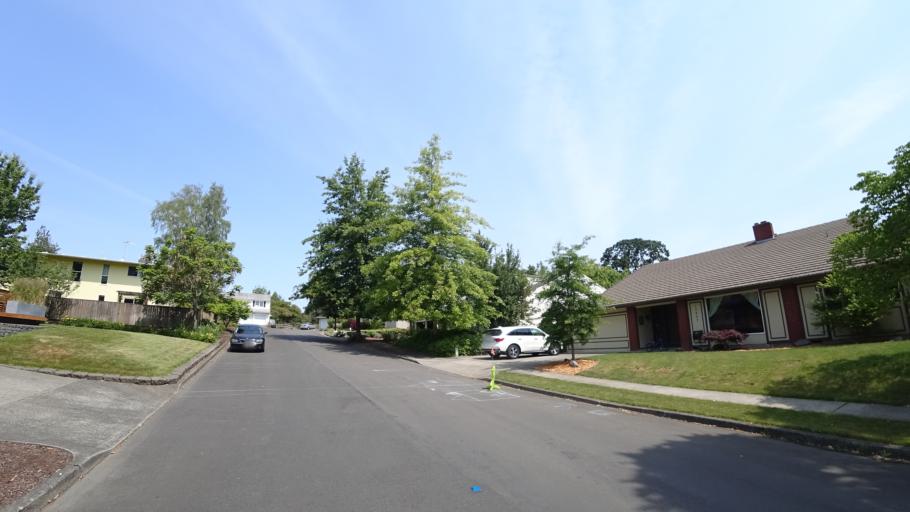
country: US
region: Oregon
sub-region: Washington County
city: Oak Hills
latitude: 45.5383
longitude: -122.8300
